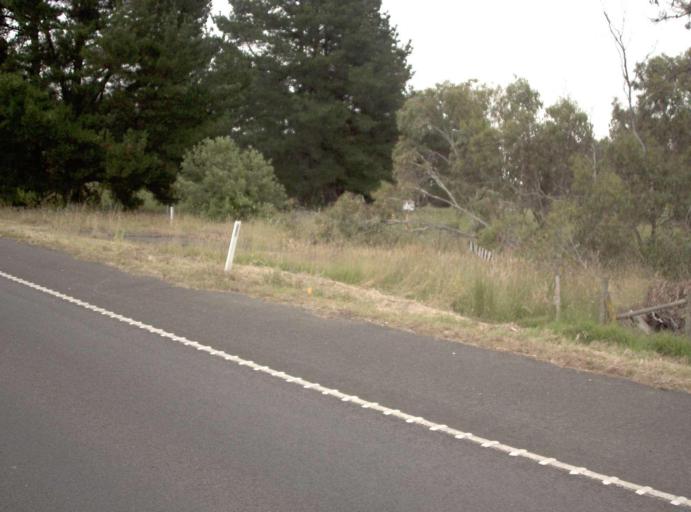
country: AU
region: Victoria
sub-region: Latrobe
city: Morwell
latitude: -38.2818
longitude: 146.4118
